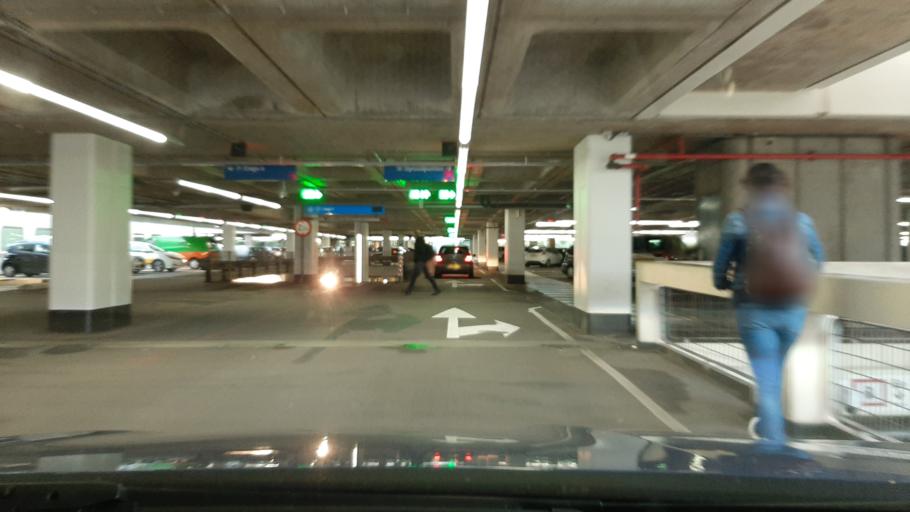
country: NL
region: South Holland
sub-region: Gemeente Rotterdam
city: Rotterdam
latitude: 51.9103
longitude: 4.4706
